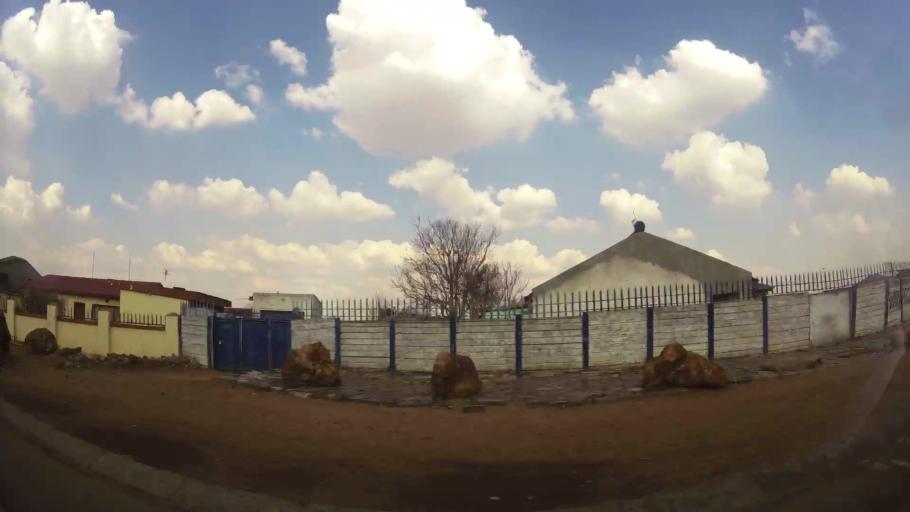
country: ZA
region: Gauteng
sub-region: Ekurhuleni Metropolitan Municipality
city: Germiston
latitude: -26.3452
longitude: 28.1559
